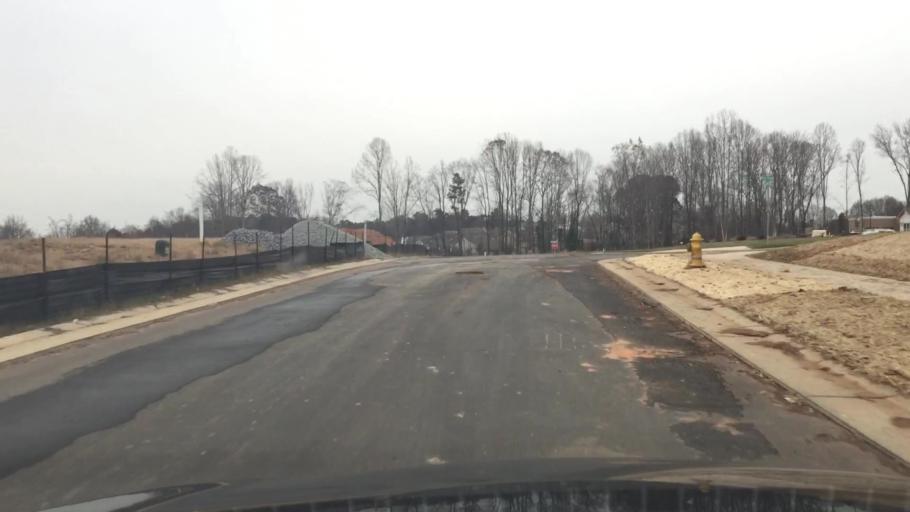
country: US
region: North Carolina
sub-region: Iredell County
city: Mooresville
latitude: 35.5803
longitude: -80.7921
